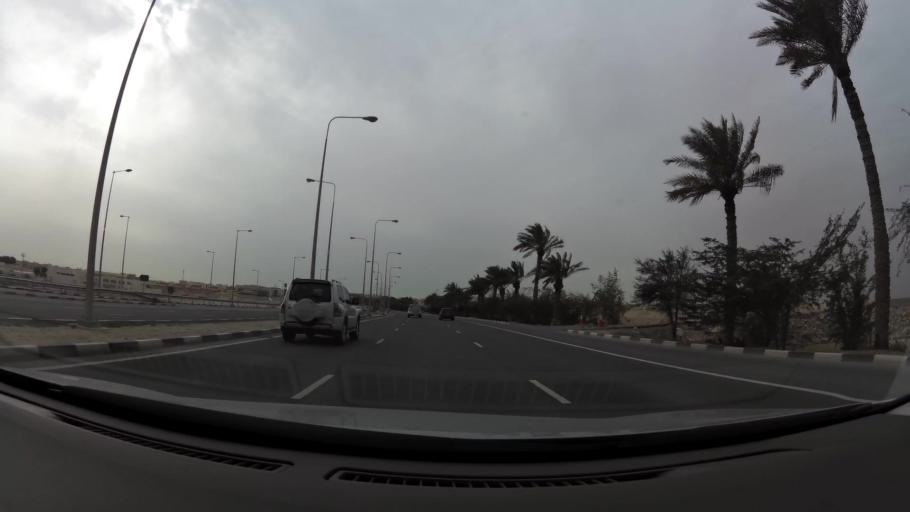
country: QA
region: Baladiyat ad Dawhah
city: Doha
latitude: 25.3340
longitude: 51.4964
